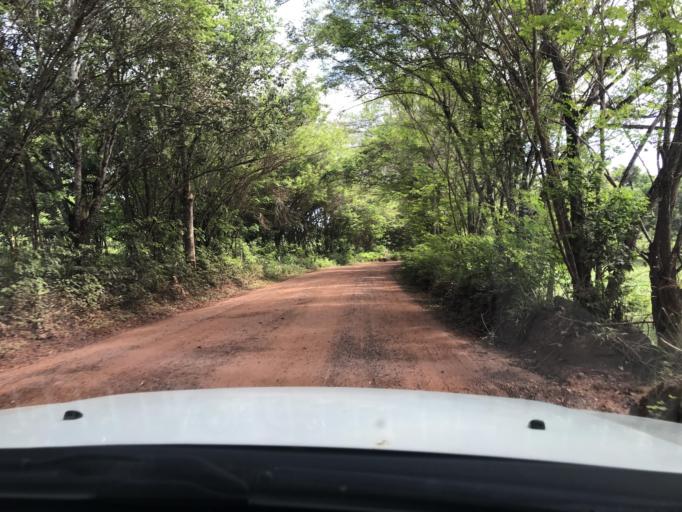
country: BR
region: Bahia
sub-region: Entre Rios
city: Entre Rios
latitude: -12.1768
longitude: -38.1204
